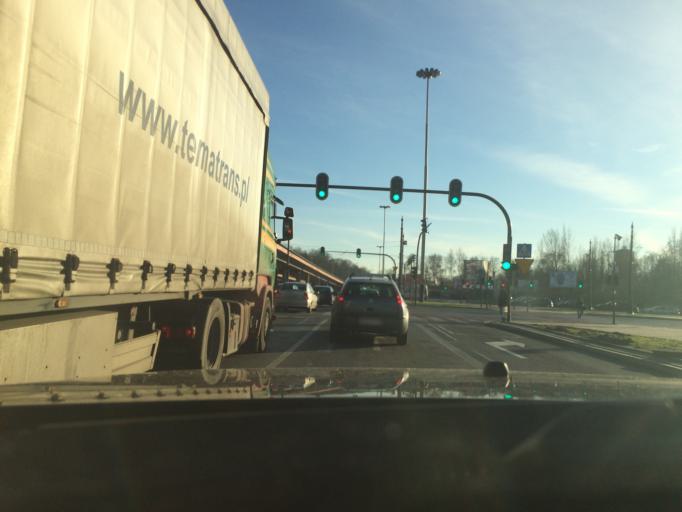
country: PL
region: Lodz Voivodeship
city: Lodz
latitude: 51.7567
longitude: 19.4341
